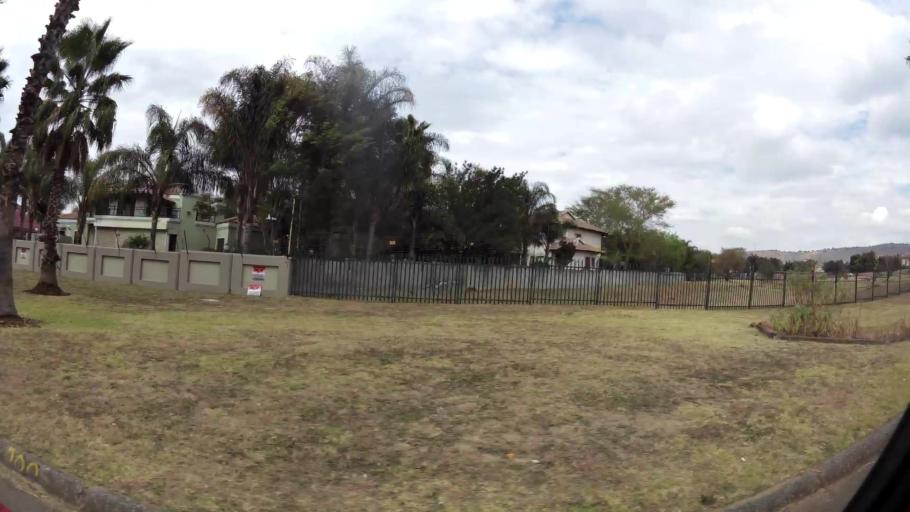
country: ZA
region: Gauteng
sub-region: West Rand District Municipality
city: Muldersdriseloop
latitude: -26.0767
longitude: 27.8618
